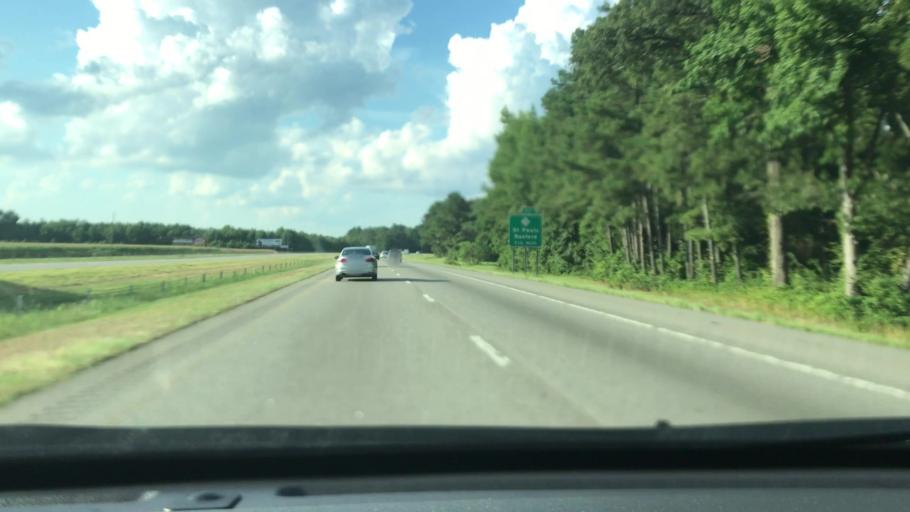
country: US
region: North Carolina
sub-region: Robeson County
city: Saint Pauls
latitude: 34.7886
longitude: -78.9945
